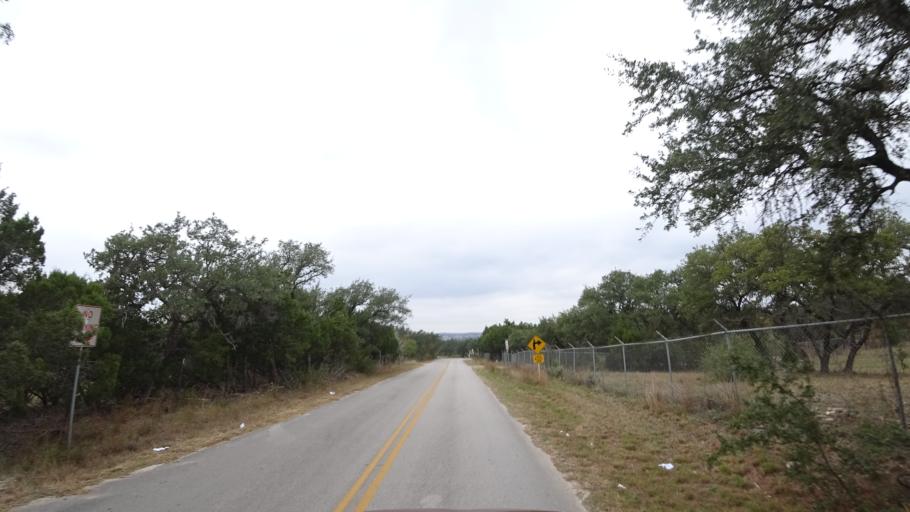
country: US
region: Texas
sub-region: Williamson County
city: Anderson Mill
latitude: 30.4467
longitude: -97.8352
